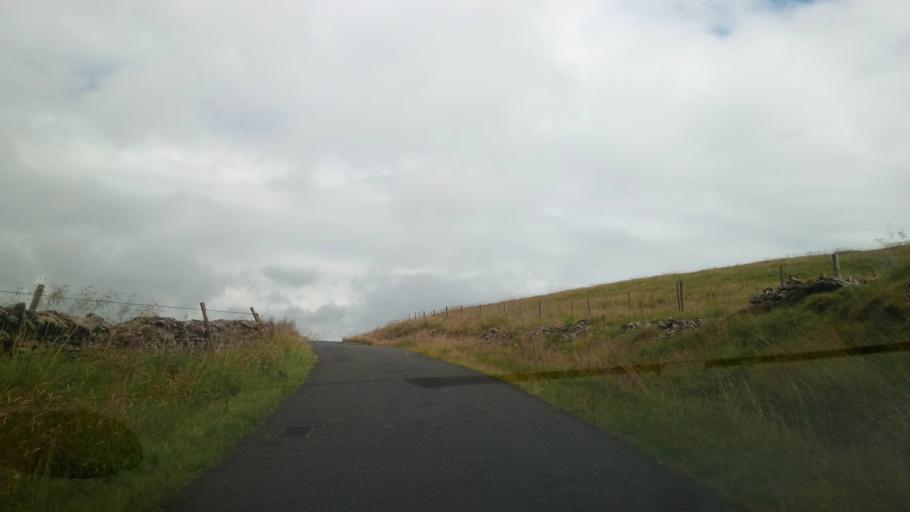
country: GB
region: England
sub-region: Cumbria
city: Kirkby Stephen
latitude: 54.2902
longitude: -2.3374
